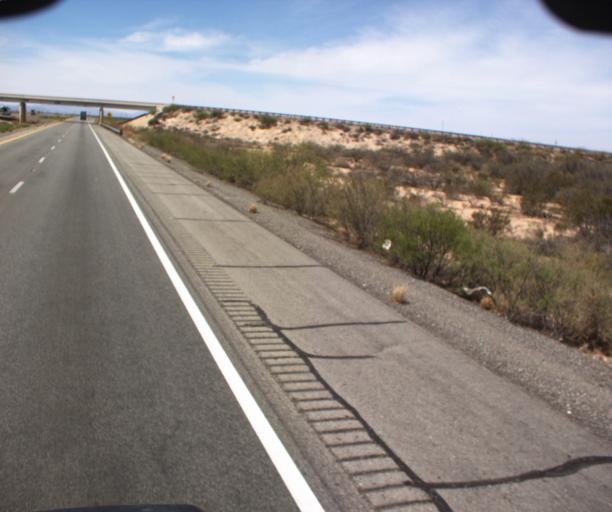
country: US
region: New Mexico
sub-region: Hidalgo County
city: Lordsburg
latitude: 32.2711
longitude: -109.2475
